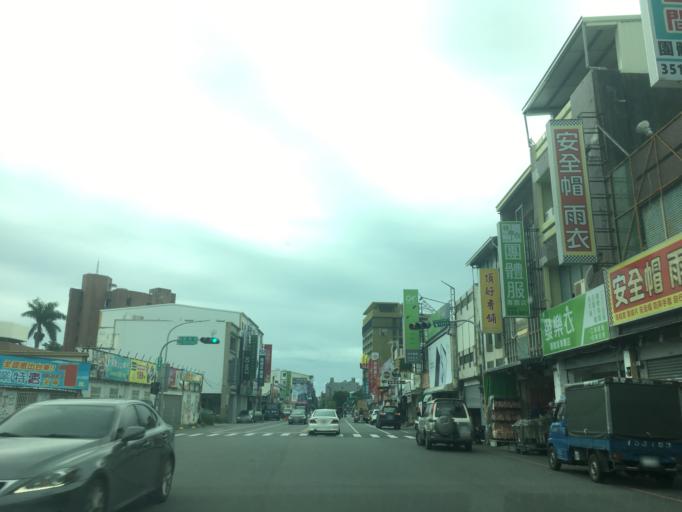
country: TW
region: Taiwan
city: Taitung City
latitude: 22.7566
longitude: 121.1437
